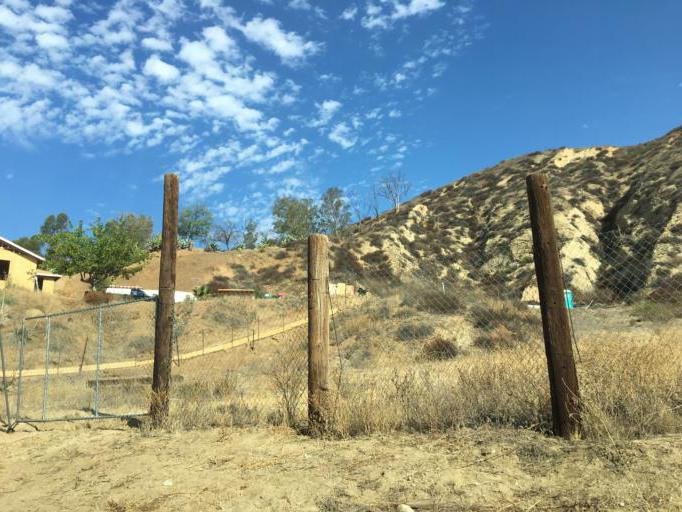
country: US
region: California
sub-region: Los Angeles County
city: Val Verde
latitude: 34.4502
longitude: -118.6585
